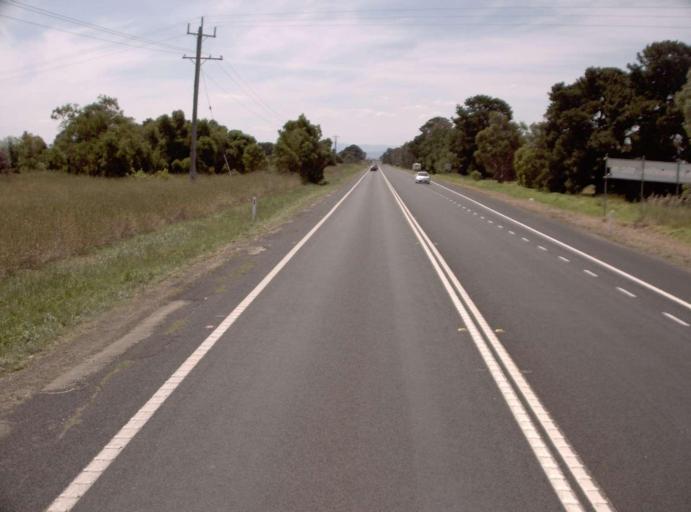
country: AU
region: Victoria
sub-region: Wellington
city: Sale
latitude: -38.0474
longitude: 147.0646
